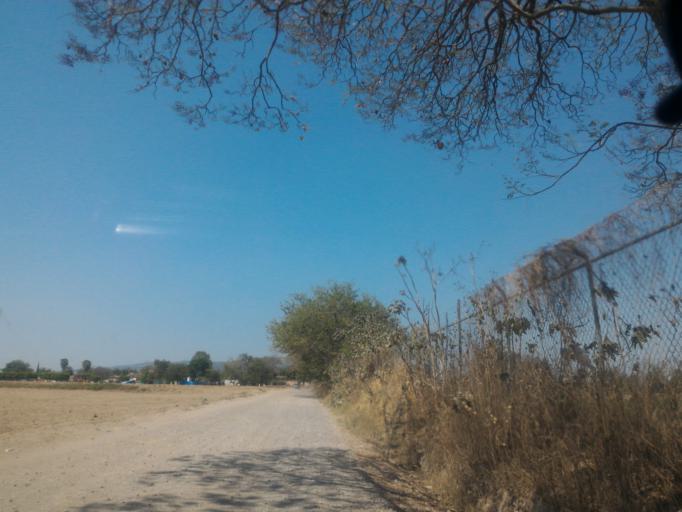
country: MX
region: Jalisco
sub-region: San Pedro Tlaquepaque
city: Paseo del Prado
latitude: 20.5644
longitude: -103.4062
